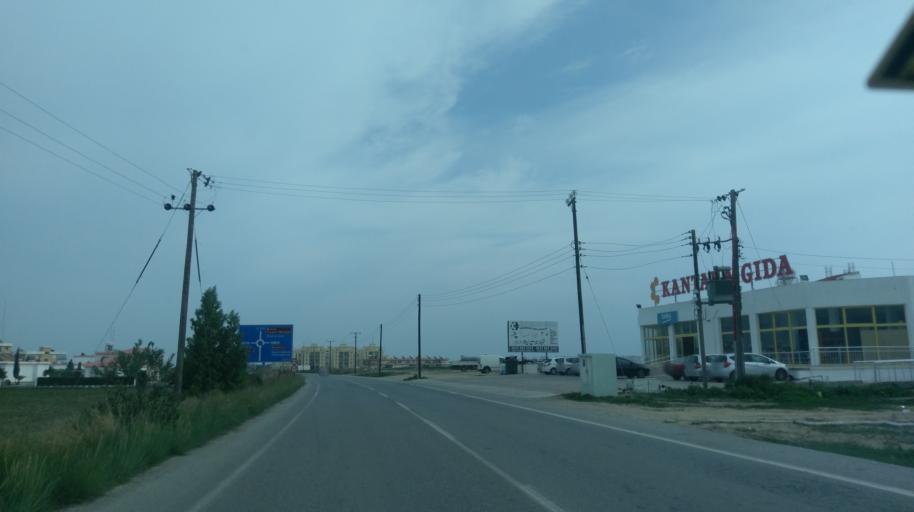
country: CY
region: Ammochostos
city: Trikomo
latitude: 35.2785
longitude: 33.8933
